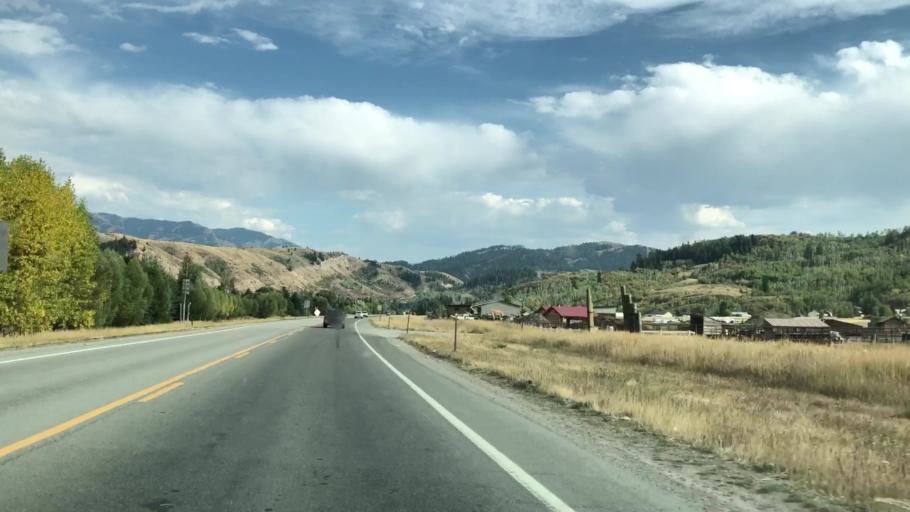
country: US
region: Wyoming
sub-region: Teton County
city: South Park
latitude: 43.3691
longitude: -110.7371
